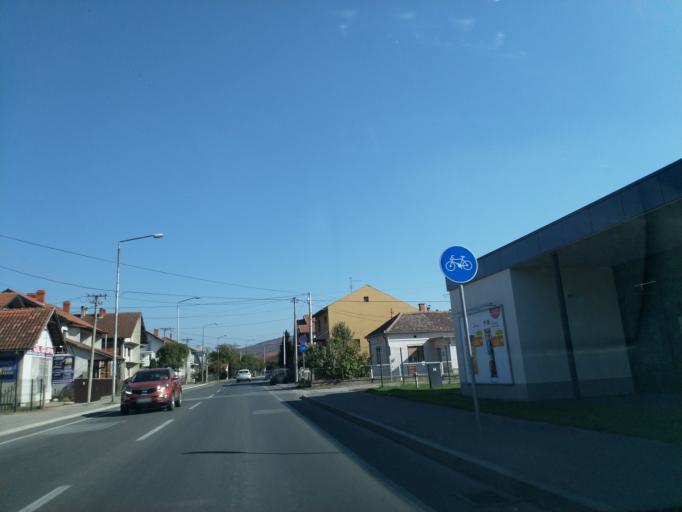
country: RS
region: Central Serbia
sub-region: Pomoravski Okrug
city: Paracin
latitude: 43.8599
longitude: 21.4234
